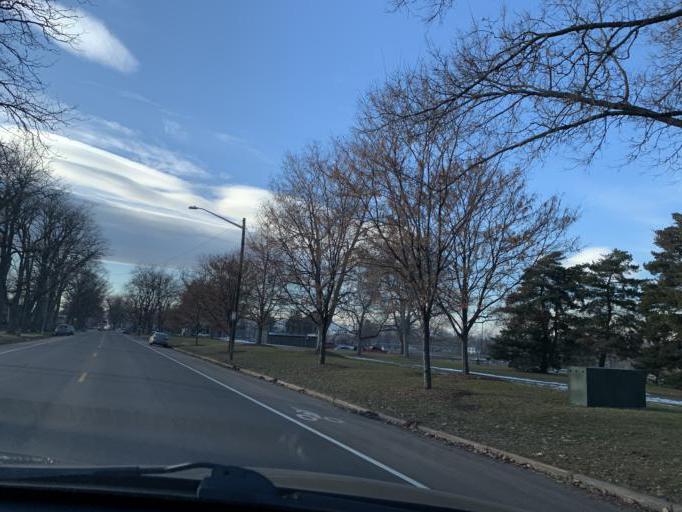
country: US
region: Colorado
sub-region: Adams County
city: Berkley
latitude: 39.7803
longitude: -105.0315
